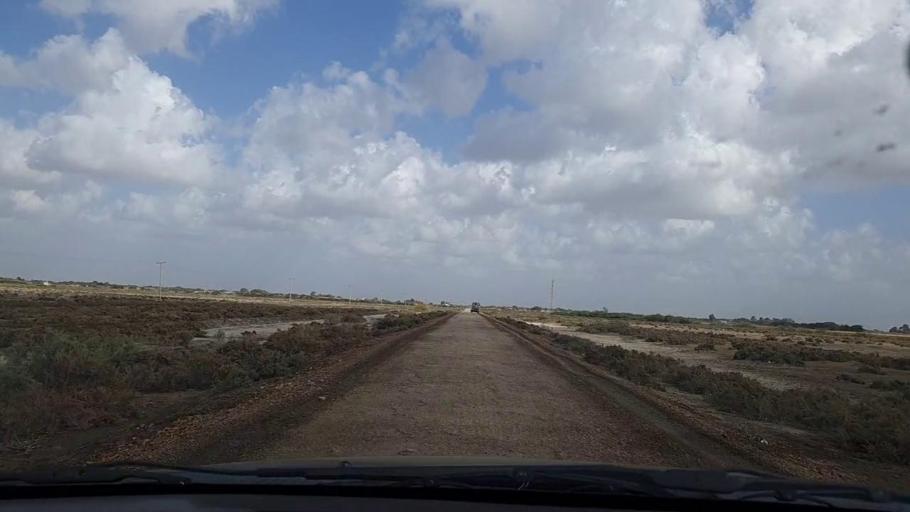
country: PK
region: Sindh
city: Keti Bandar
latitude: 24.1052
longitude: 67.5906
